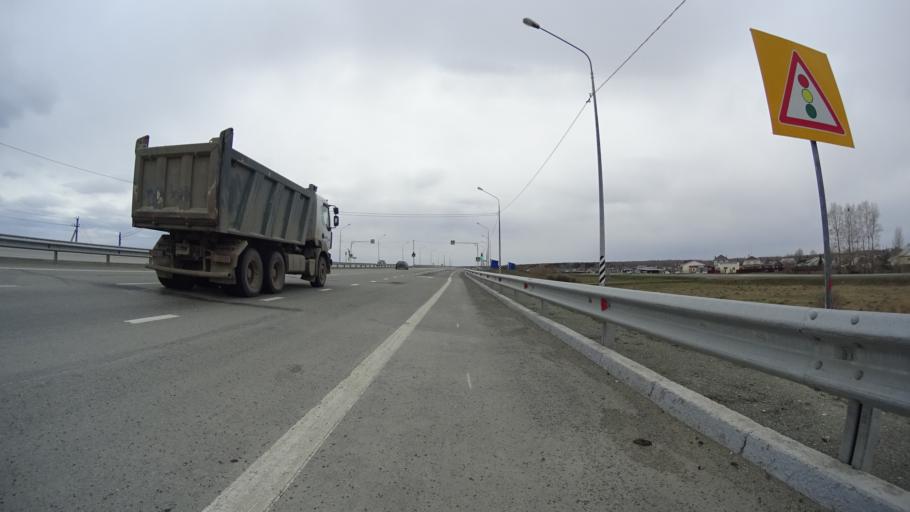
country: RU
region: Chelyabinsk
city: Yemanzhelinka
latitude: 54.7973
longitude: 61.3074
